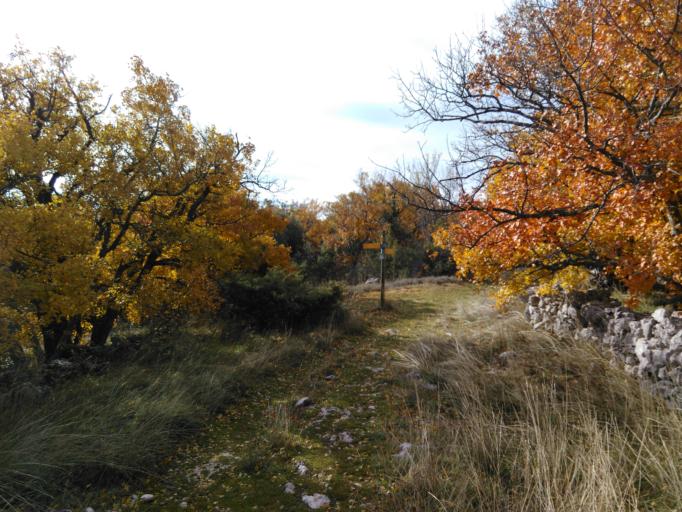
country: FR
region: Provence-Alpes-Cote d'Azur
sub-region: Departement du Vaucluse
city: Saint-Saturnin-les-Apt
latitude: 44.0170
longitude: 5.3289
